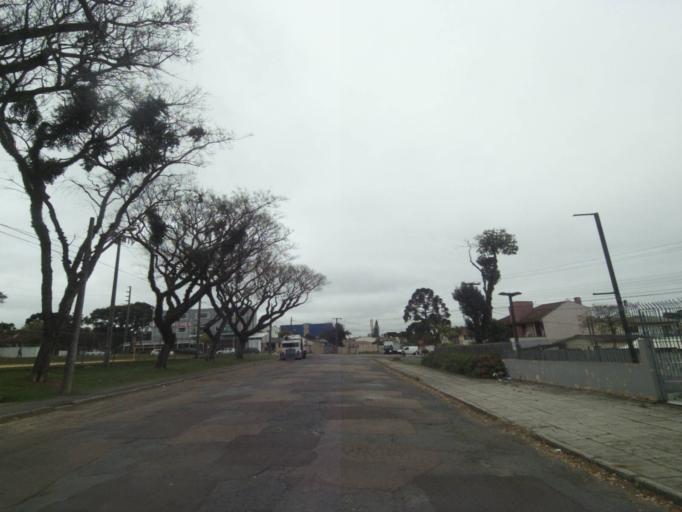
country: BR
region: Parana
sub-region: Curitiba
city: Curitiba
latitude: -25.4709
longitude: -49.2765
